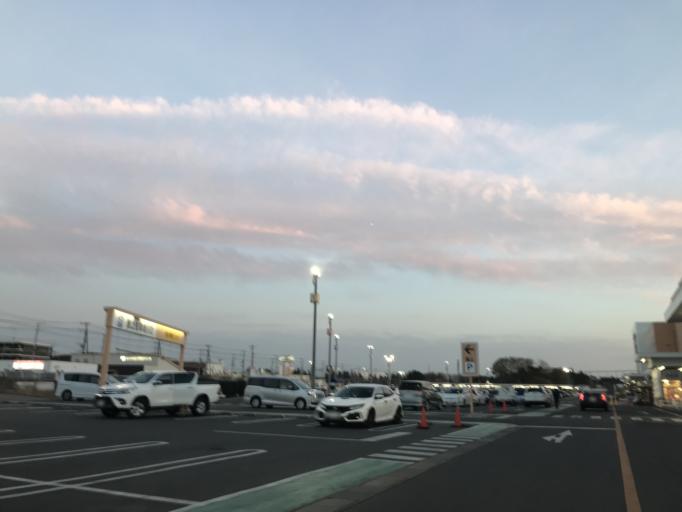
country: JP
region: Ibaraki
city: Naka
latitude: 36.0774
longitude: 140.0715
